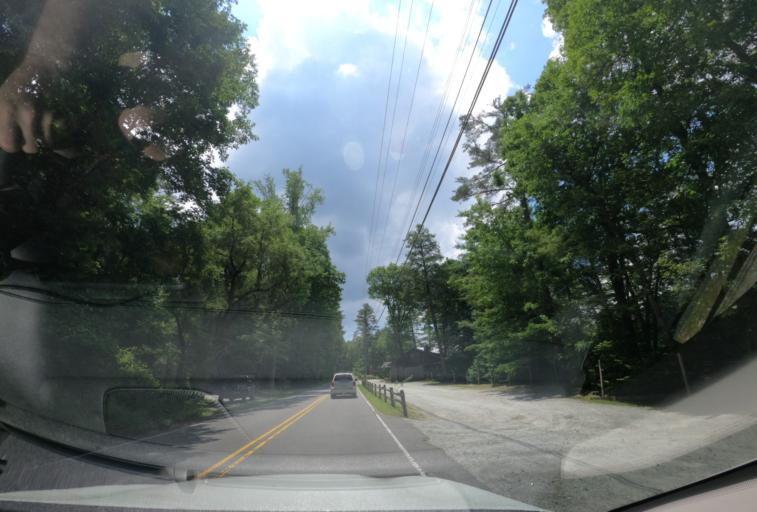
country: US
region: North Carolina
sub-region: Macon County
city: Franklin
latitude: 35.0640
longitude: -83.2199
